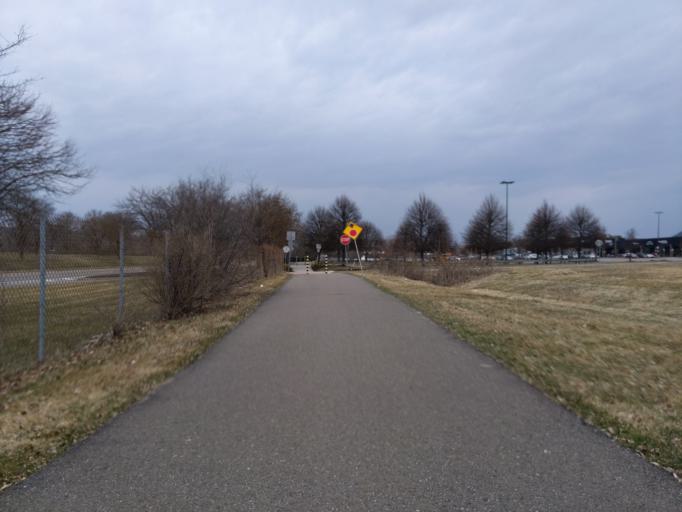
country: US
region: New York
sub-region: Chemung County
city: Elmira
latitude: 42.1032
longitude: -76.8092
